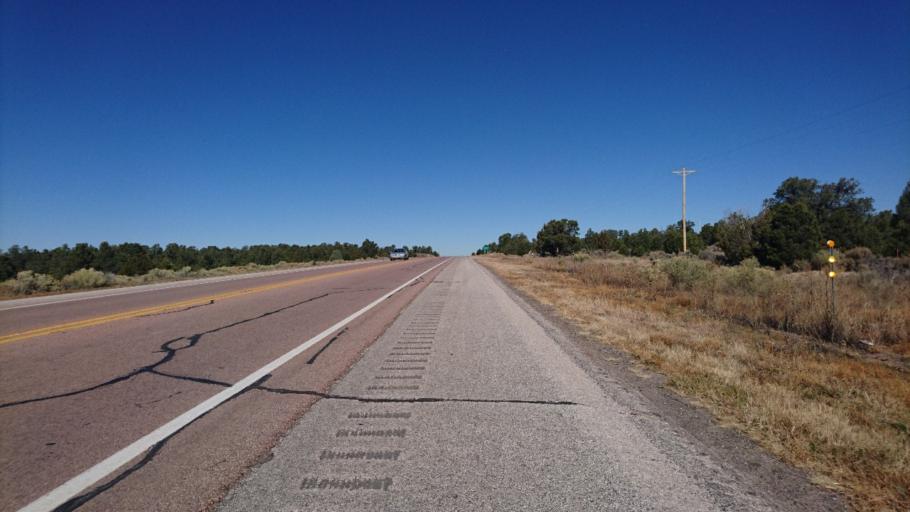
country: US
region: New Mexico
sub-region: McKinley County
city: Gallup
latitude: 35.3086
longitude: -108.7576
